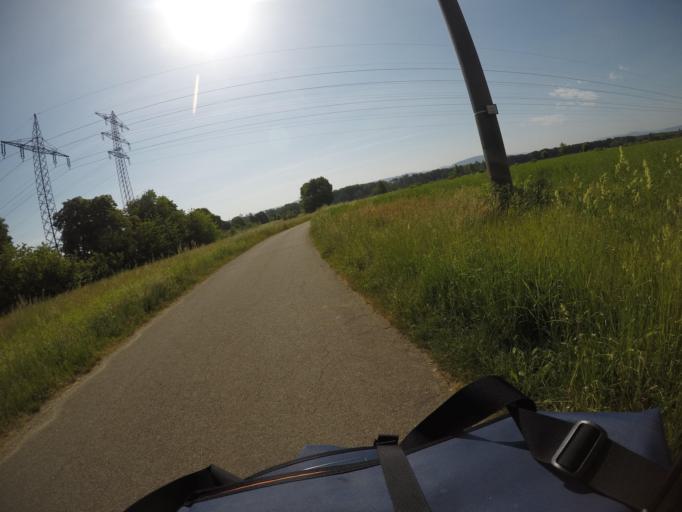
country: DE
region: Baden-Wuerttemberg
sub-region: Karlsruhe Region
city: Durmersheim
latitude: 48.9100
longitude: 8.2783
